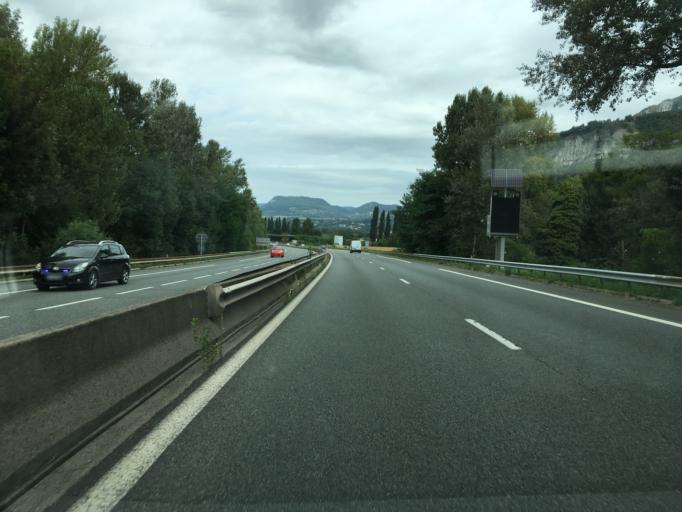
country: FR
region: Rhone-Alpes
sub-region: Departement de l'Isere
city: Voreppe
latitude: 45.3016
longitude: 5.6217
